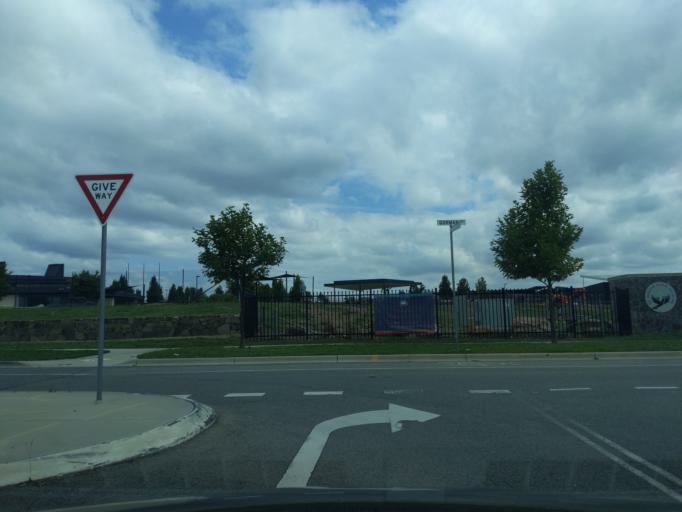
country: AU
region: New South Wales
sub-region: Queanbeyan
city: Queanbeyan
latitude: -35.4217
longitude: 149.2337
